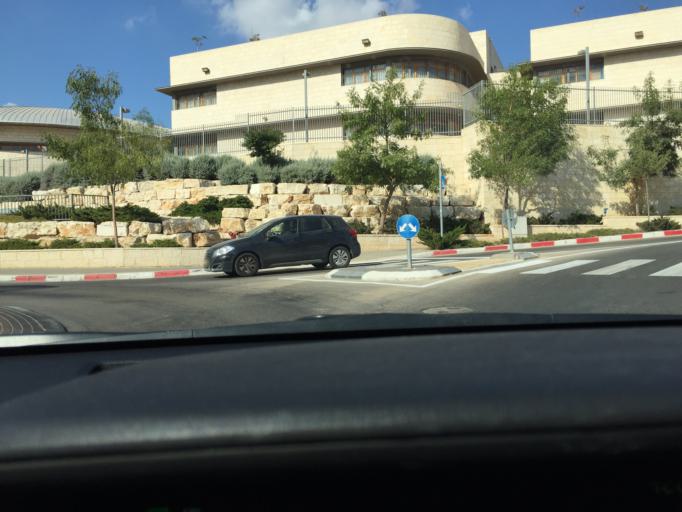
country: PS
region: West Bank
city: Budrus
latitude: 32.0042
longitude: 34.9494
